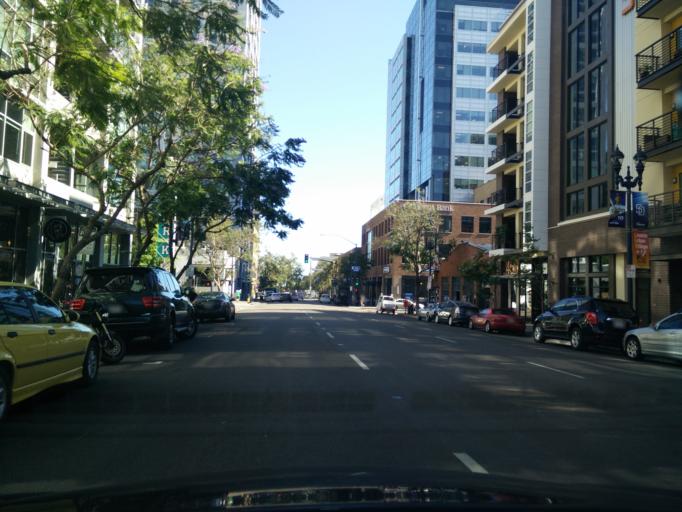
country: US
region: California
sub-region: San Diego County
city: San Diego
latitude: 32.7100
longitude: -117.1555
